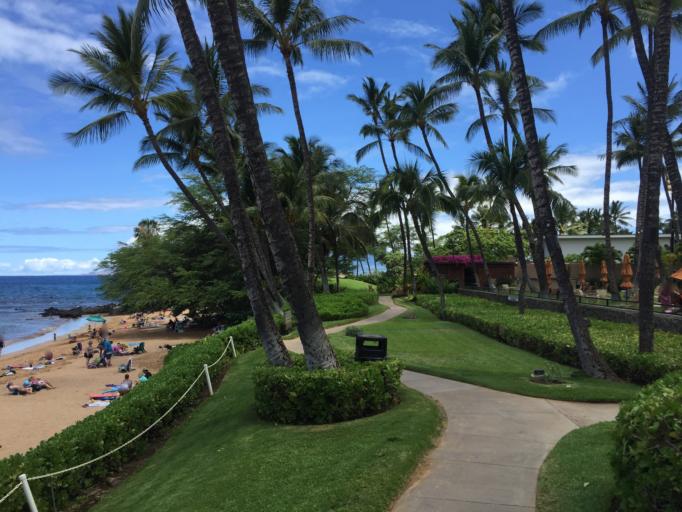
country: US
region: Hawaii
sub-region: Maui County
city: Kihei
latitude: 20.6909
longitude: -156.4436
